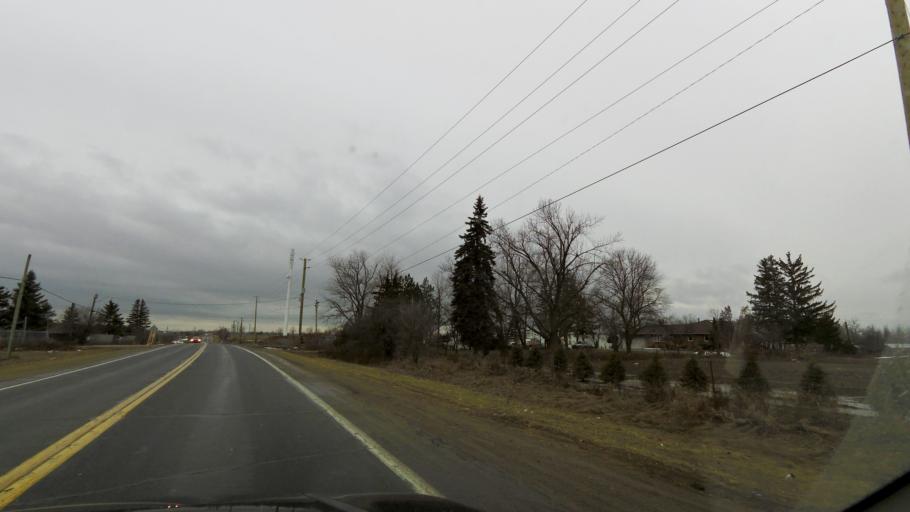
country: CA
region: Ontario
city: Vaughan
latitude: 43.8404
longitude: -79.6711
